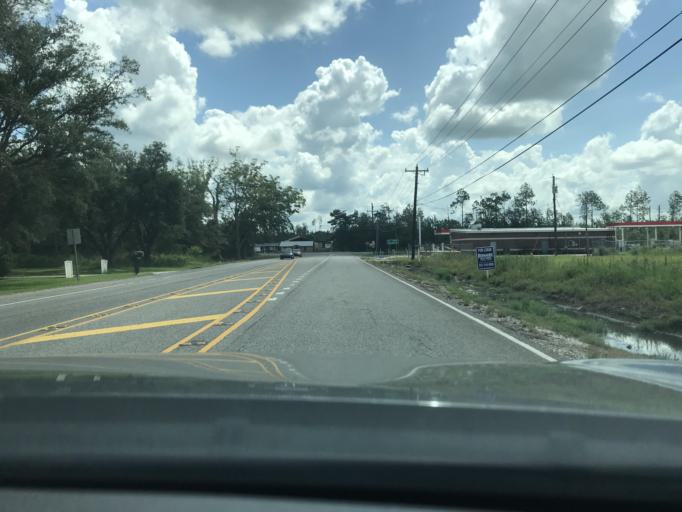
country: US
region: Louisiana
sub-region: Calcasieu Parish
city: Moss Bluff
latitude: 30.3445
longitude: -93.2020
